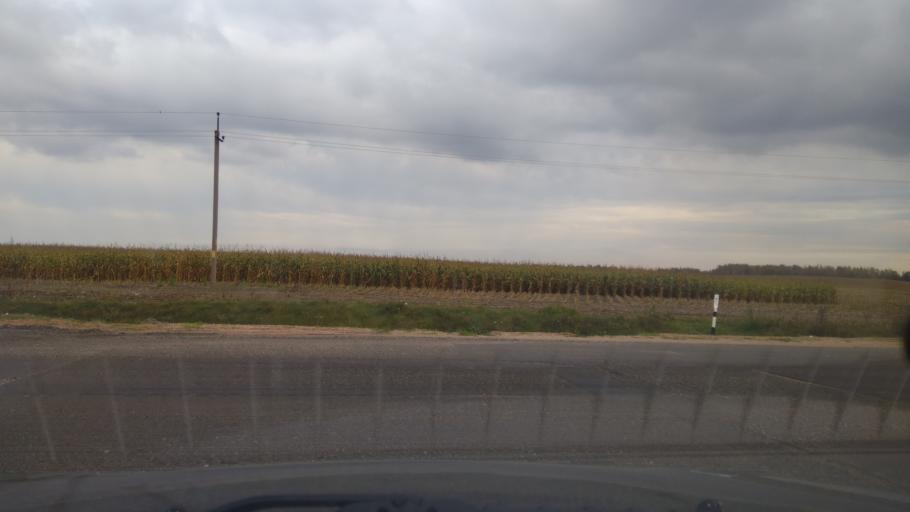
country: BY
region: Minsk
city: Dukora
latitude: 53.6552
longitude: 27.9446
